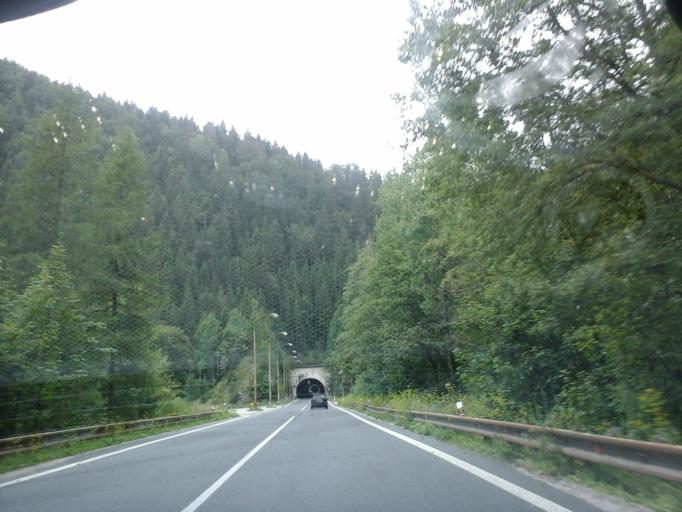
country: SK
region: Kosicky
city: Dobsina
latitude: 48.8731
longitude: 20.3307
